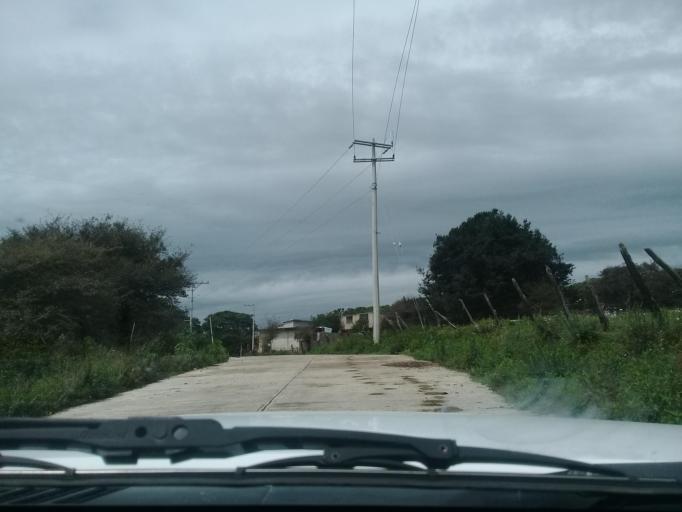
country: MX
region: Veracruz
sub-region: Rafael Lucio
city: Piletas
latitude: 19.5958
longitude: -96.9816
